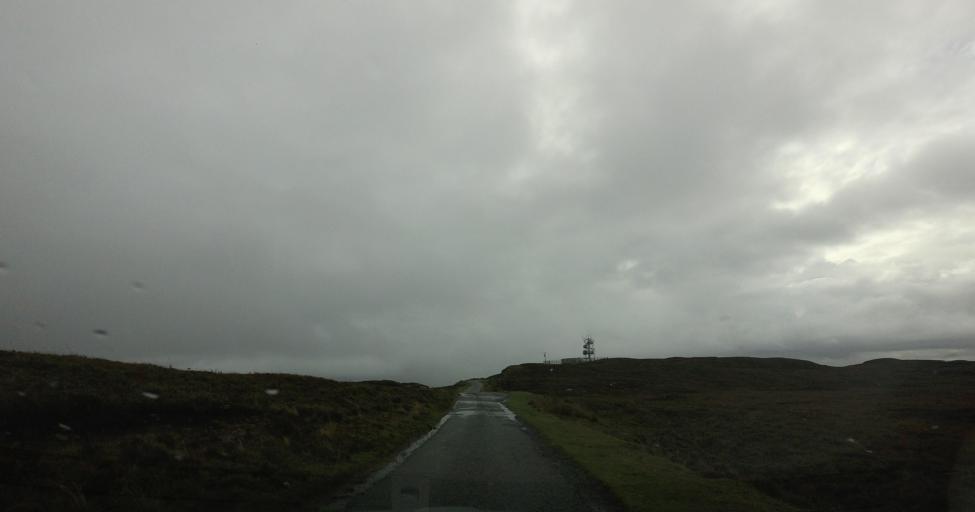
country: GB
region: Scotland
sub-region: Highland
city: Isle of Skye
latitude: 57.1438
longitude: -6.0834
